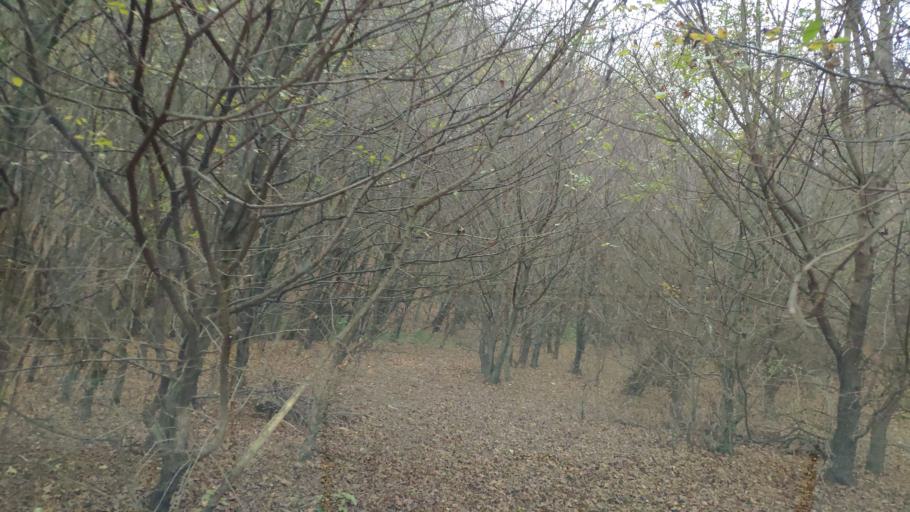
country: SK
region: Presovsky
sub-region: Okres Presov
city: Presov
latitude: 48.9403
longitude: 21.1336
